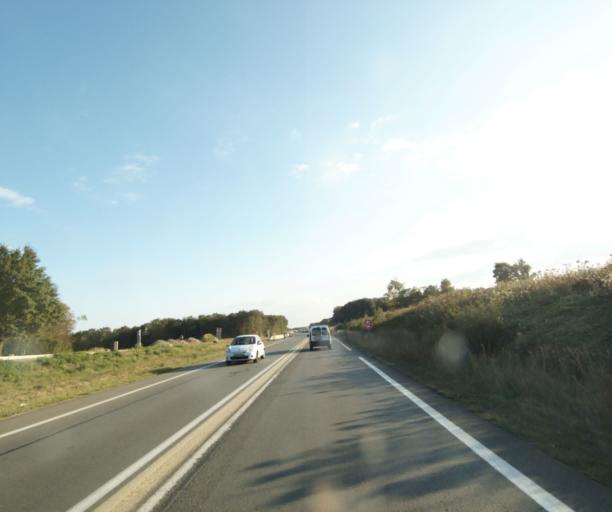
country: FR
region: Bourgogne
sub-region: Departement de Saone-et-Loire
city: Palinges
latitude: 46.5228
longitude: 4.1646
